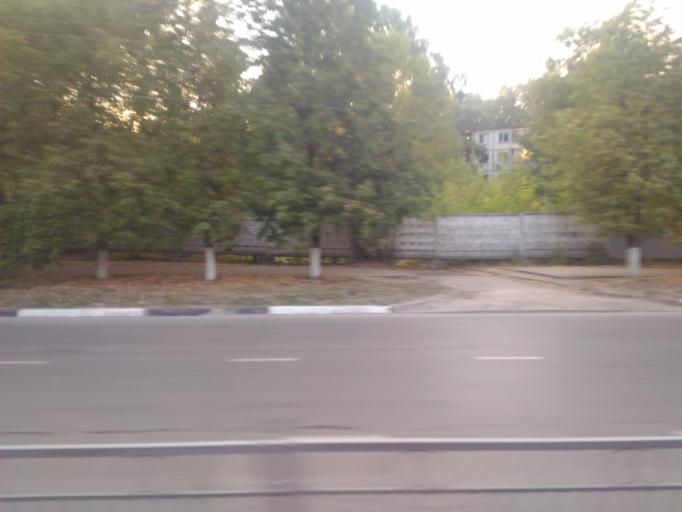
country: RU
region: Ulyanovsk
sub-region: Ulyanovskiy Rayon
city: Ulyanovsk
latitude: 54.2880
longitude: 48.3040
